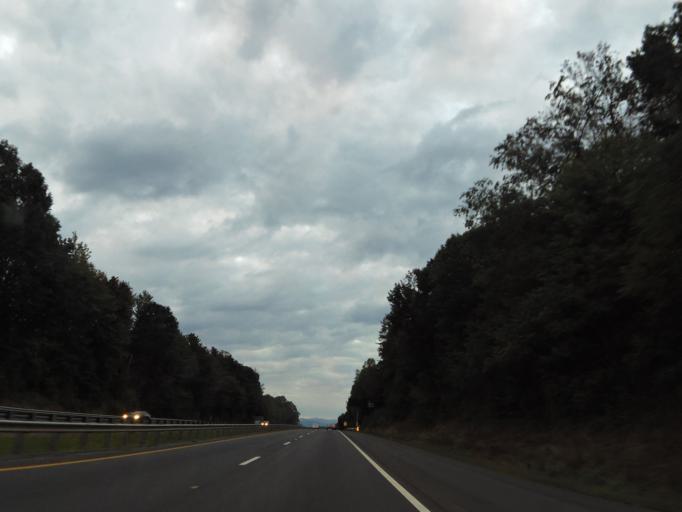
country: US
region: North Carolina
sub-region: Buncombe County
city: Weaverville
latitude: 35.6780
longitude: -82.5824
